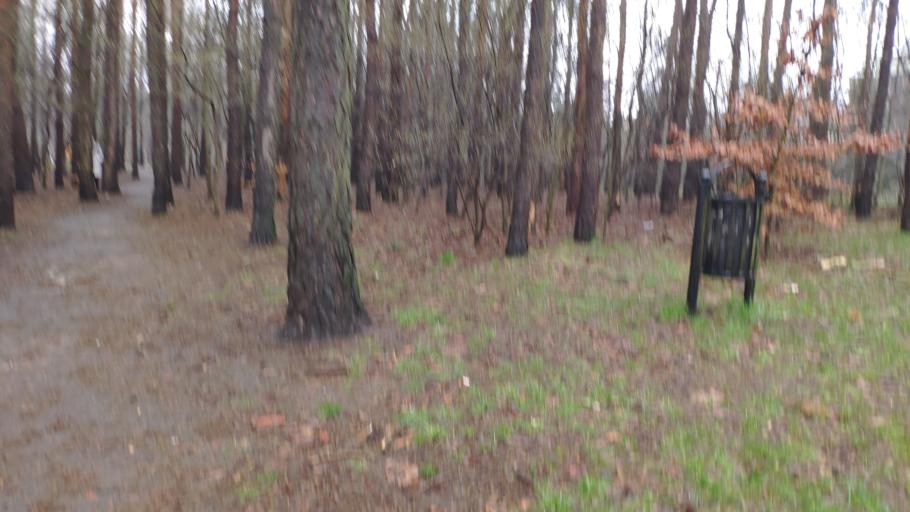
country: PL
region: Lodz Voivodeship
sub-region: Powiat lodzki wschodni
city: Andrespol
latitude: 51.7516
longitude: 19.5685
